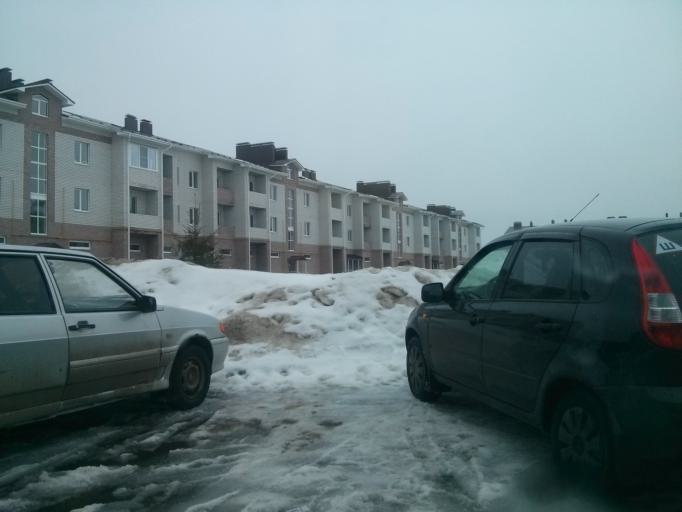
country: RU
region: Vladimir
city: Murom
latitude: 55.5458
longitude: 42.0581
